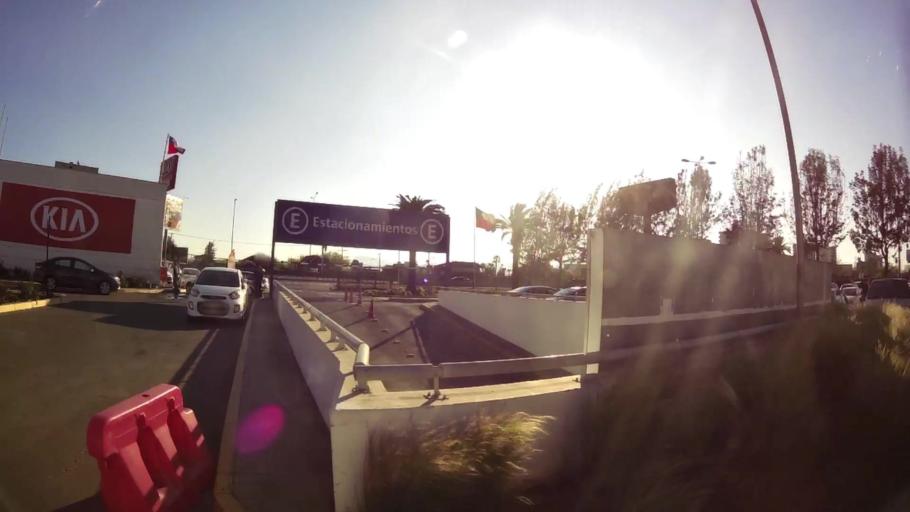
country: CL
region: Santiago Metropolitan
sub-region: Provincia de Santiago
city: Lo Prado
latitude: -33.4846
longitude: -70.7516
